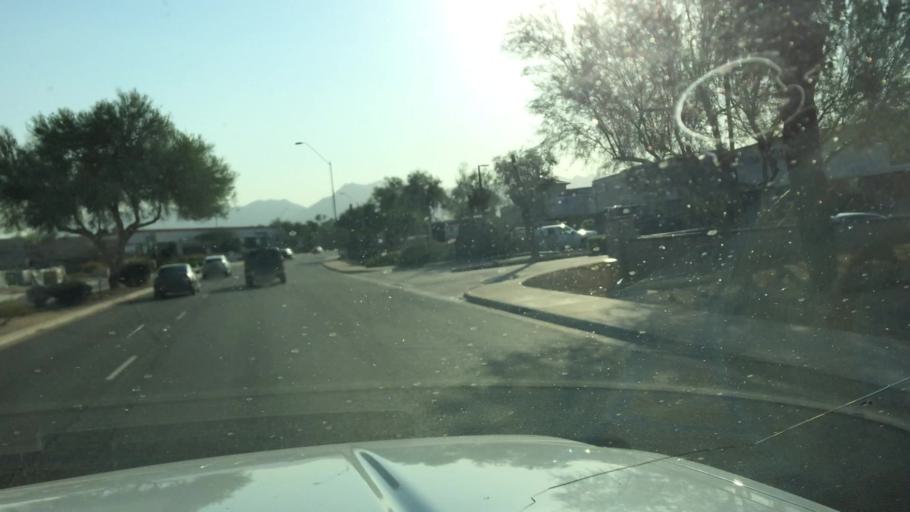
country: US
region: Arizona
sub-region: Maricopa County
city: Paradise Valley
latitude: 33.6266
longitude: -111.9215
